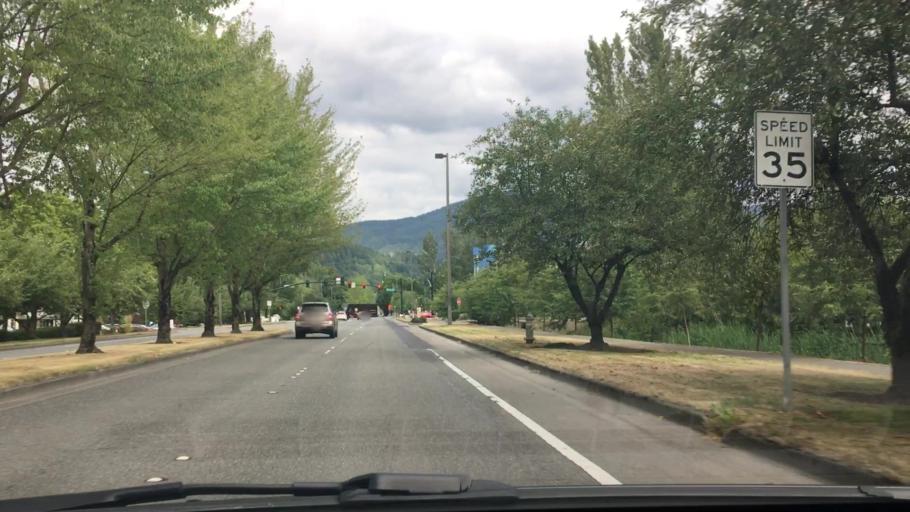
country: US
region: Washington
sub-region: King County
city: Issaquah
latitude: 47.5439
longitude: -122.0489
